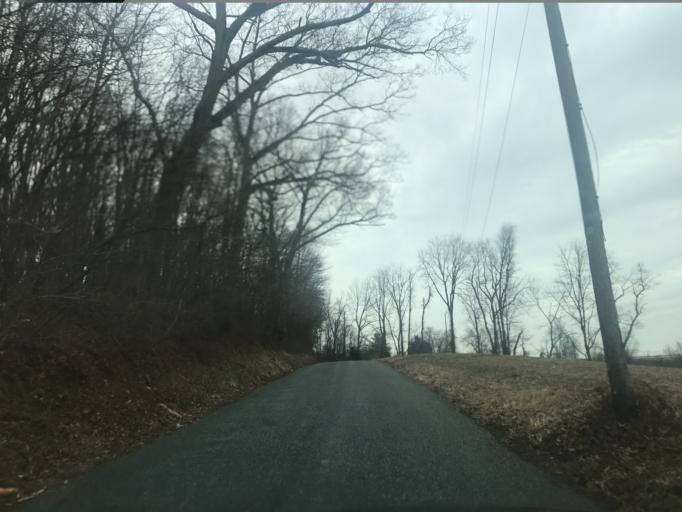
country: US
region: Maryland
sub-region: Harford County
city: Jarrettsville
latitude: 39.6733
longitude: -76.4129
